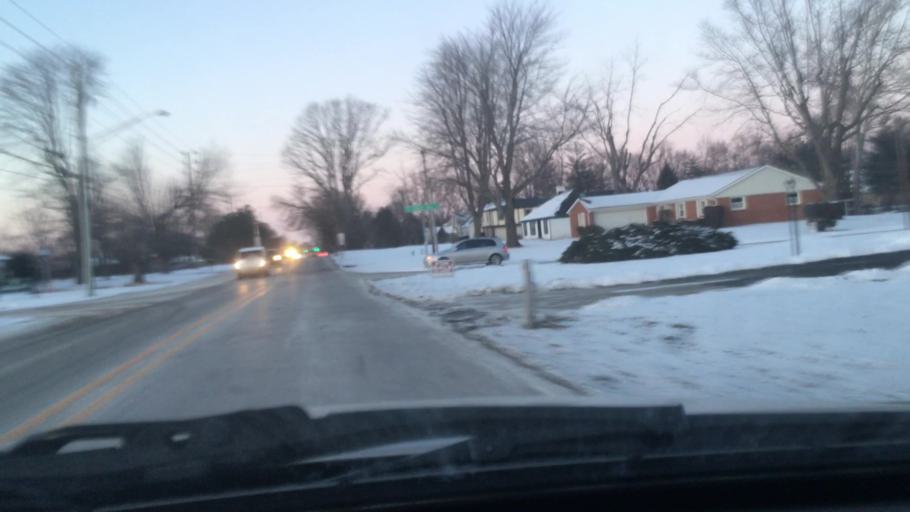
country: US
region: Indiana
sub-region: Marion County
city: Lawrence
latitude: 39.8863
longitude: -86.0330
